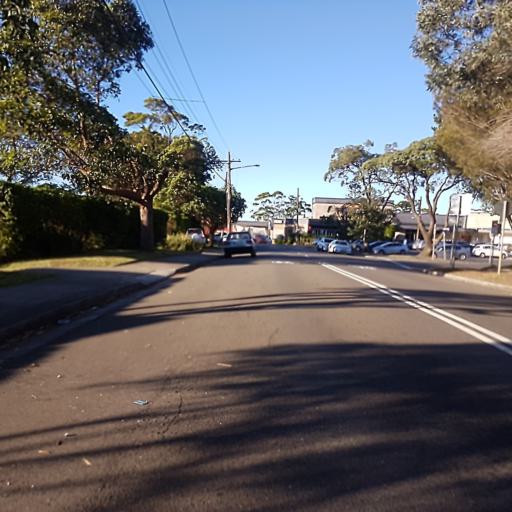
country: AU
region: New South Wales
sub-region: Warringah
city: Forestville
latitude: -33.7514
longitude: 151.2234
